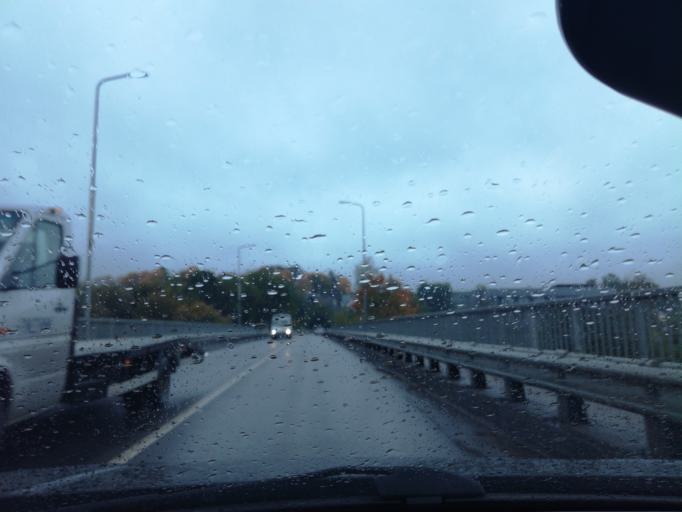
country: LT
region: Alytaus apskritis
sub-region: Alytus
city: Alytus
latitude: 54.4015
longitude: 24.0549
